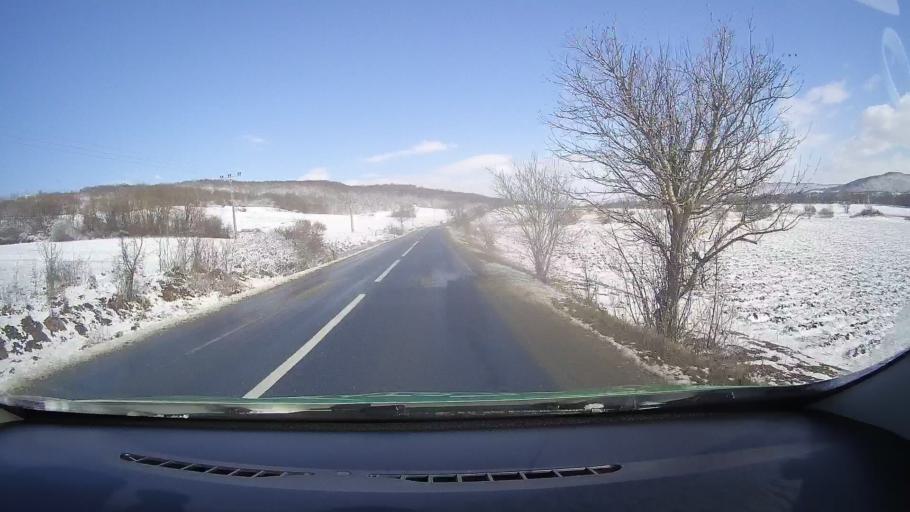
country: RO
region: Sibiu
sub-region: Comuna Rosia
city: Rosia
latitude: 45.8238
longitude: 24.3843
